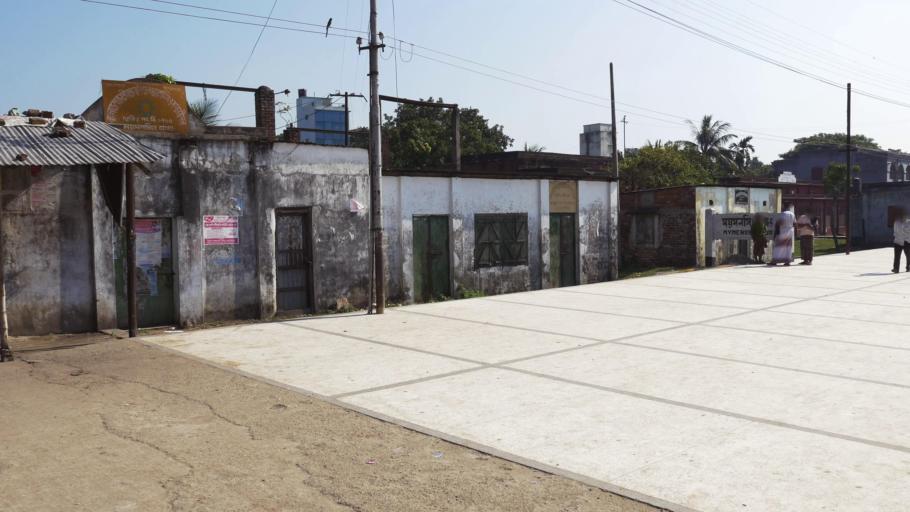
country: BD
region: Dhaka
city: Mymensingh
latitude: 24.6897
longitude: 90.4546
